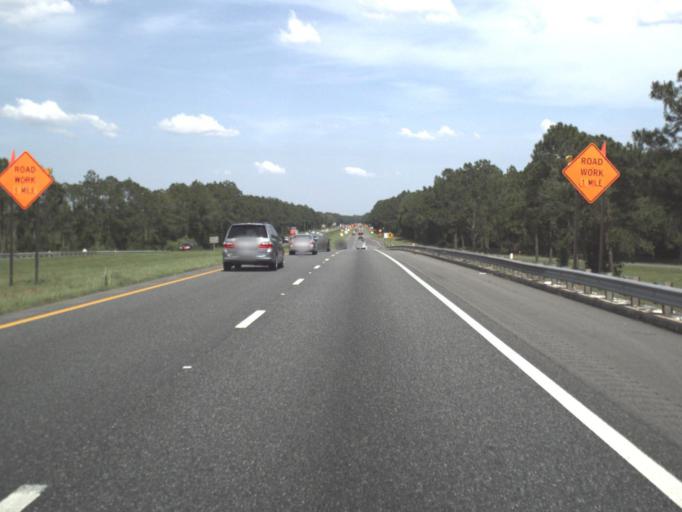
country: US
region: Florida
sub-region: Columbia County
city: Five Points
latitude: 30.2415
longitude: -82.6378
